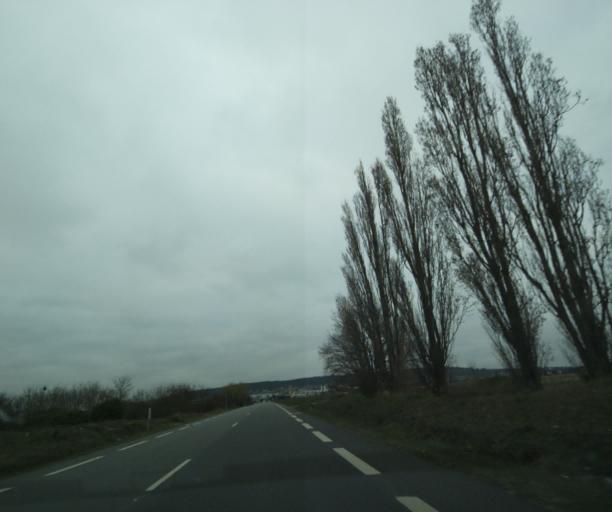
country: FR
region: Ile-de-France
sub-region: Departement des Yvelines
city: Carrieres-sous-Poissy
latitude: 48.9563
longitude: 2.0387
